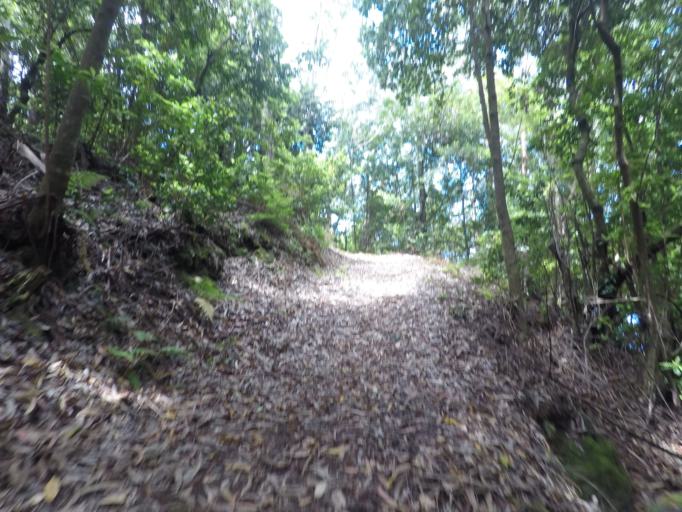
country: PT
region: Madeira
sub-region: Porto Moniz
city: Porto Moniz
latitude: 32.8345
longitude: -17.1412
